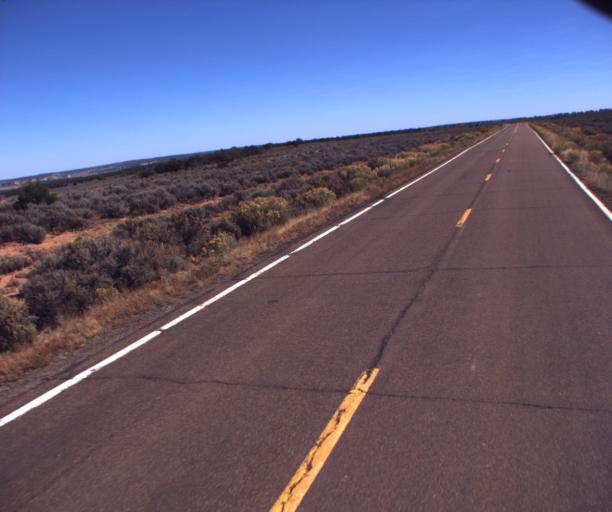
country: US
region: Arizona
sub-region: Apache County
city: Ganado
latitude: 35.7507
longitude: -109.9396
